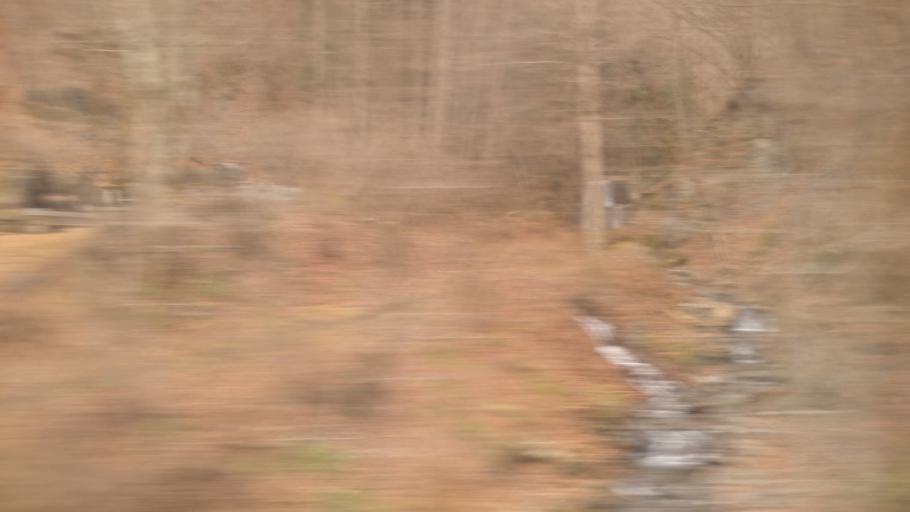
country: JP
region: Nagano
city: Tatsuno
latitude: 35.9892
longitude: 137.8469
